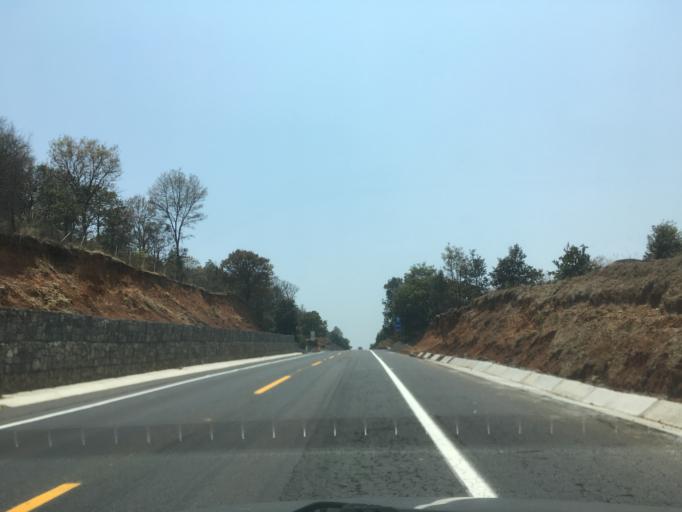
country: MX
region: Michoacan
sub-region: Patzcuaro
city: Santa Ana Chapitiro
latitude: 19.5061
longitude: -101.6784
